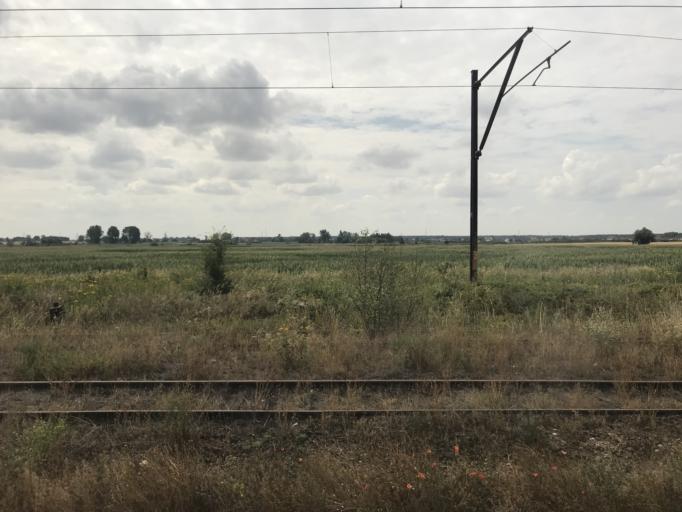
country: PL
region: Greater Poland Voivodeship
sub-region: Powiat gnieznienski
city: Gniezno
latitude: 52.5325
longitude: 17.6452
